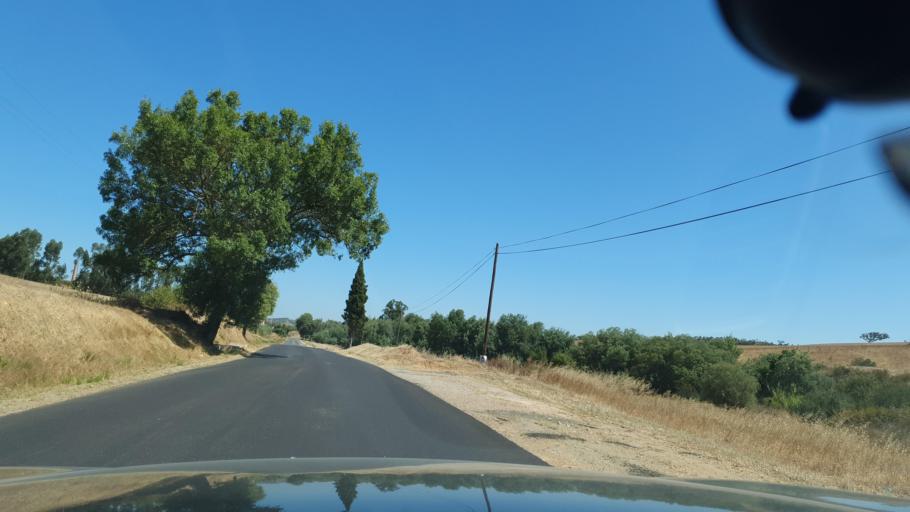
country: PT
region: Faro
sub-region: Monchique
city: Monchique
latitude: 37.4520
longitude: -8.4868
